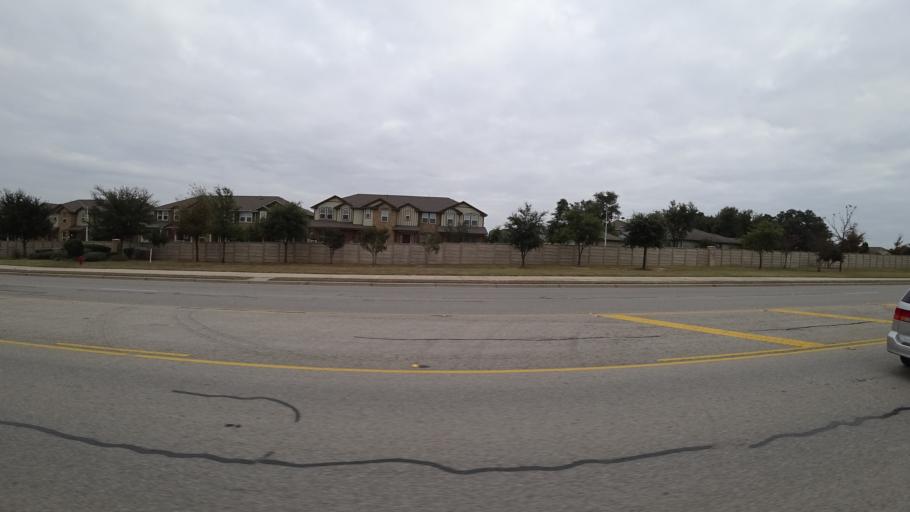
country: US
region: Texas
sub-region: Williamson County
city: Cedar Park
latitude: 30.5352
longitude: -97.8273
